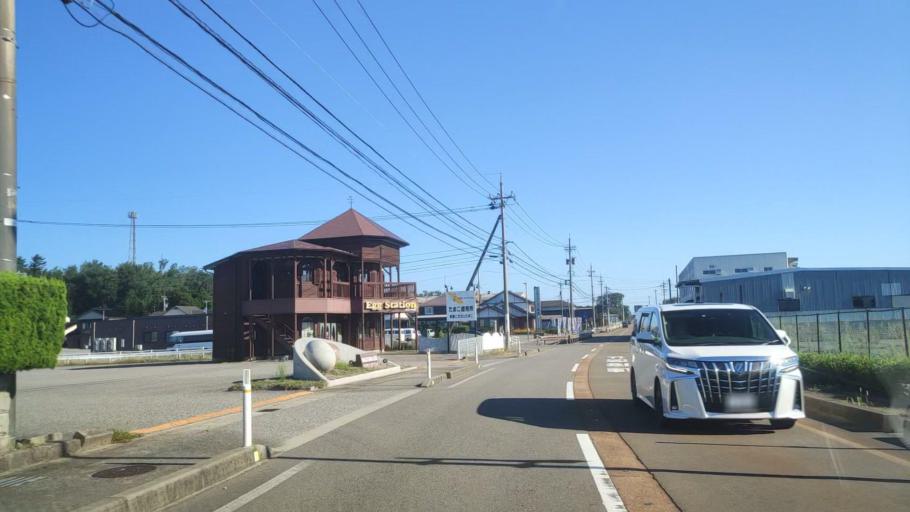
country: JP
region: Ishikawa
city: Hakui
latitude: 36.8340
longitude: 136.7609
